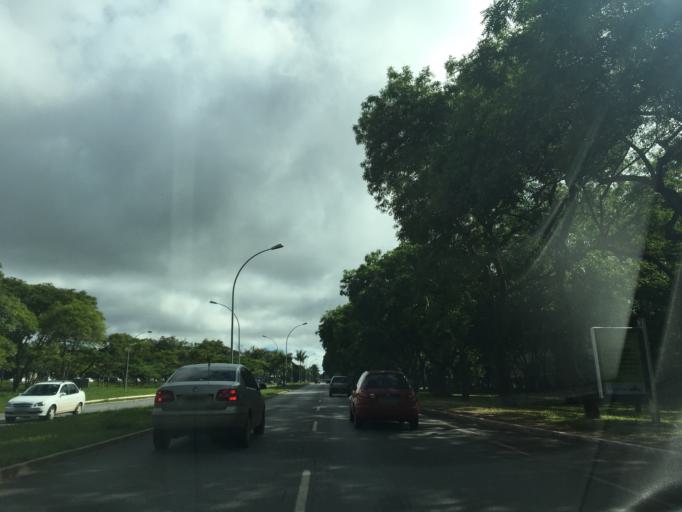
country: BR
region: Federal District
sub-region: Brasilia
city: Brasilia
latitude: -15.8251
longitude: -47.9107
